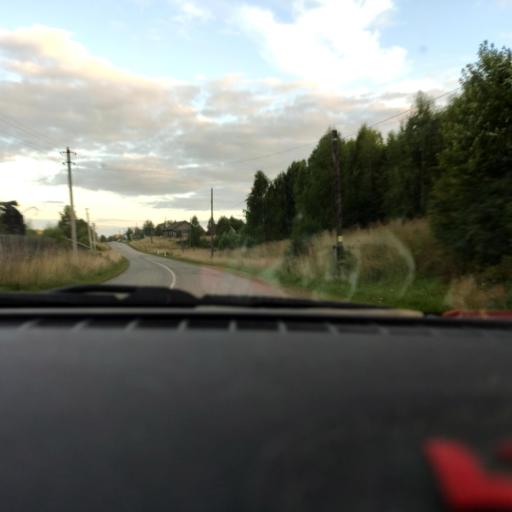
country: RU
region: Perm
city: Ocher
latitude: 57.9530
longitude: 54.8076
